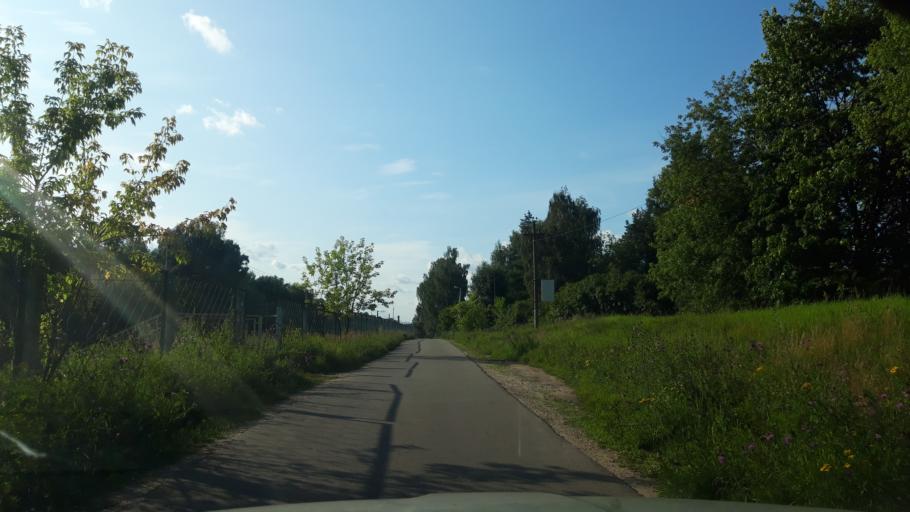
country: RU
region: Moskovskaya
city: Povarovo
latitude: 56.0630
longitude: 37.0783
